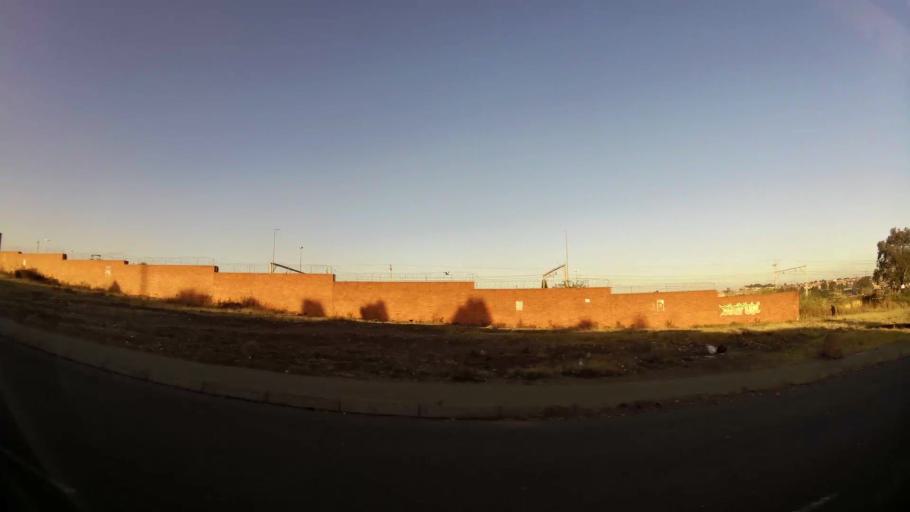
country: ZA
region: Gauteng
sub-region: Ekurhuleni Metropolitan Municipality
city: Tembisa
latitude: -26.0124
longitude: 28.2143
